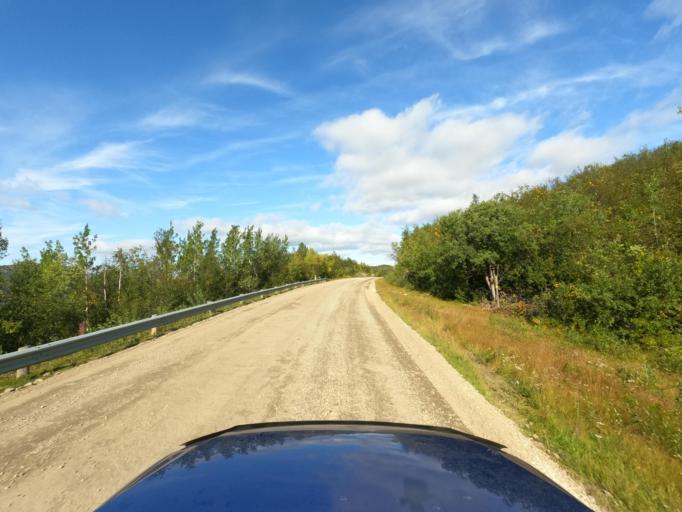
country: NO
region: Finnmark Fylke
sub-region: Porsanger
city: Lakselv
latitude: 69.8811
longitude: 25.0219
